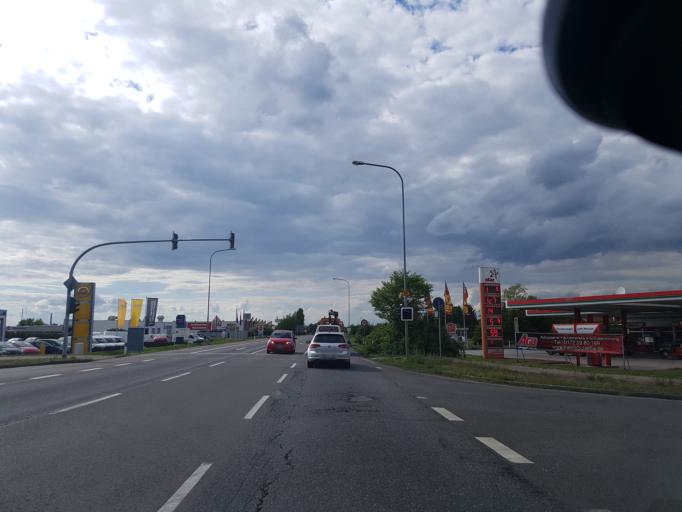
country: DE
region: Brandenburg
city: Grossraschen
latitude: 51.5799
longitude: 14.0320
